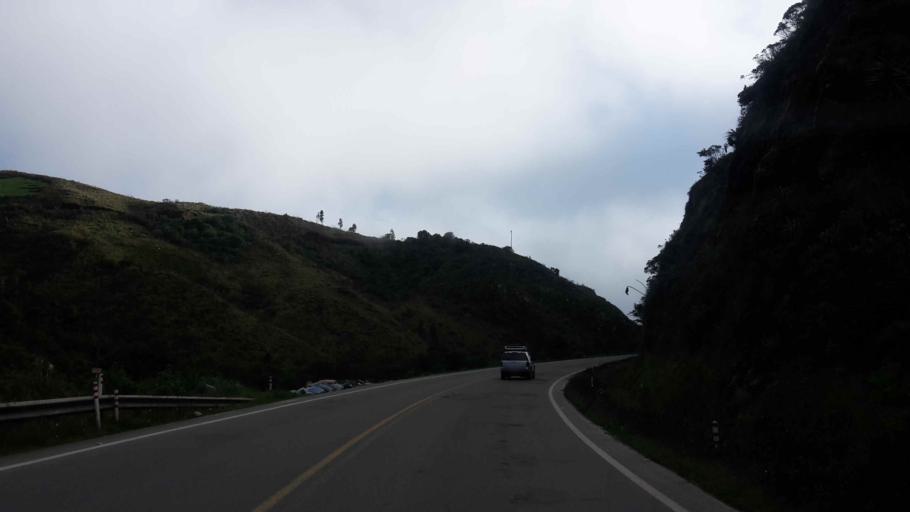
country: BO
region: Cochabamba
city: Colomi
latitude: -17.2170
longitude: -65.8918
